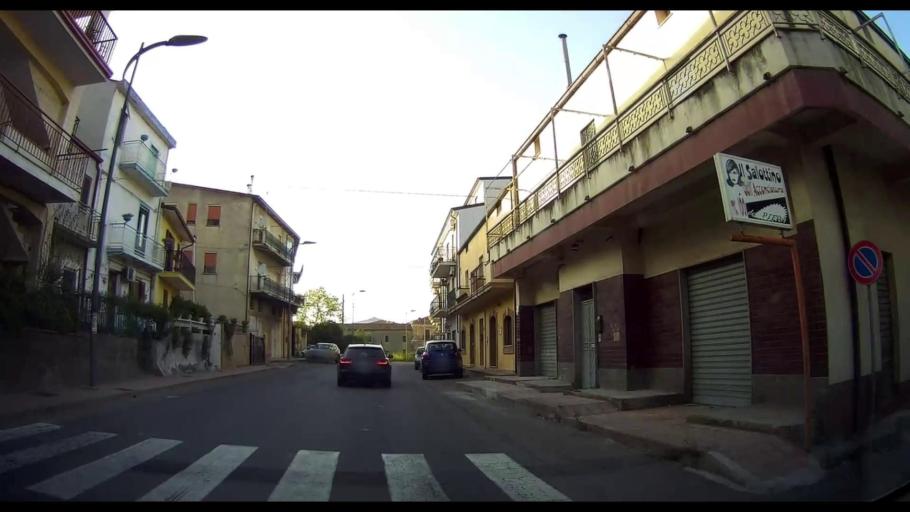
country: IT
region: Calabria
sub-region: Provincia di Crotone
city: Torretta
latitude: 39.4479
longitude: 17.0411
